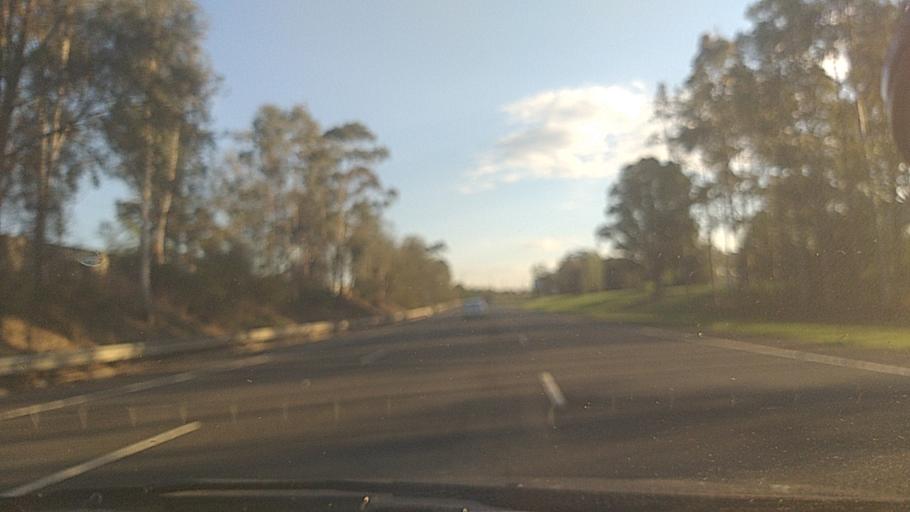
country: AU
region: New South Wales
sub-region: Camden
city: Narellan Vale
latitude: -34.0433
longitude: 150.7450
